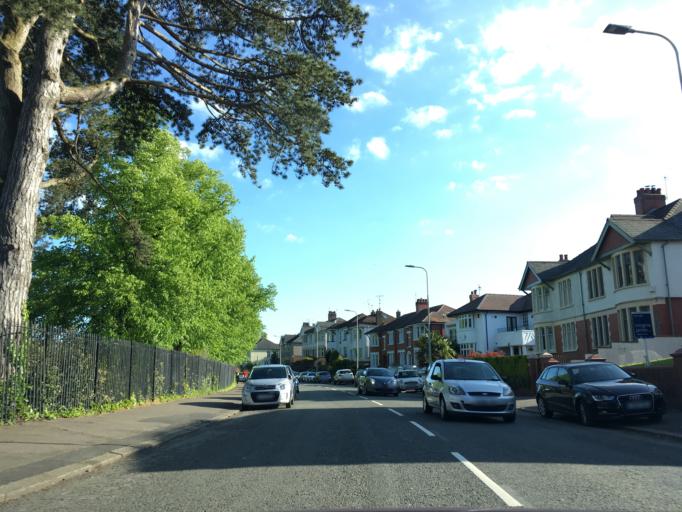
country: GB
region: Wales
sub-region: Cardiff
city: Cardiff
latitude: 51.5086
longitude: -3.1770
